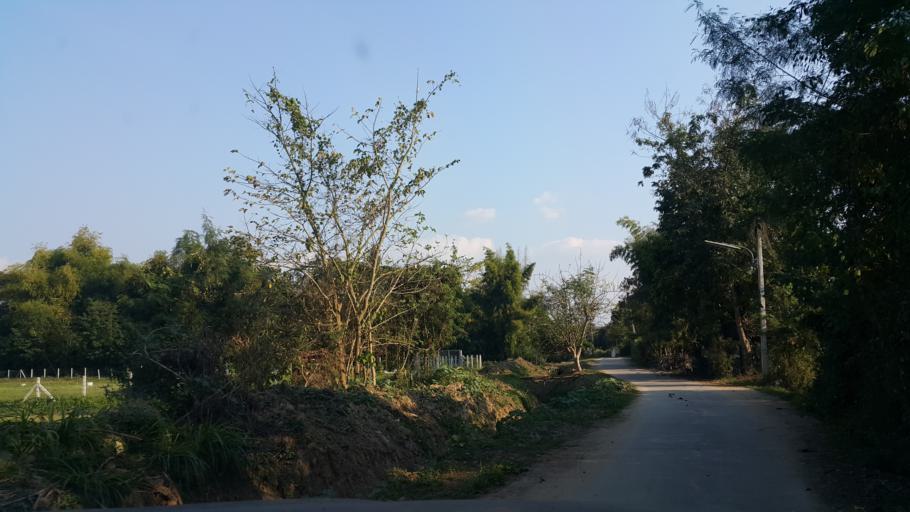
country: TH
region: Chiang Mai
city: San Kamphaeng
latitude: 18.7430
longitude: 99.1040
